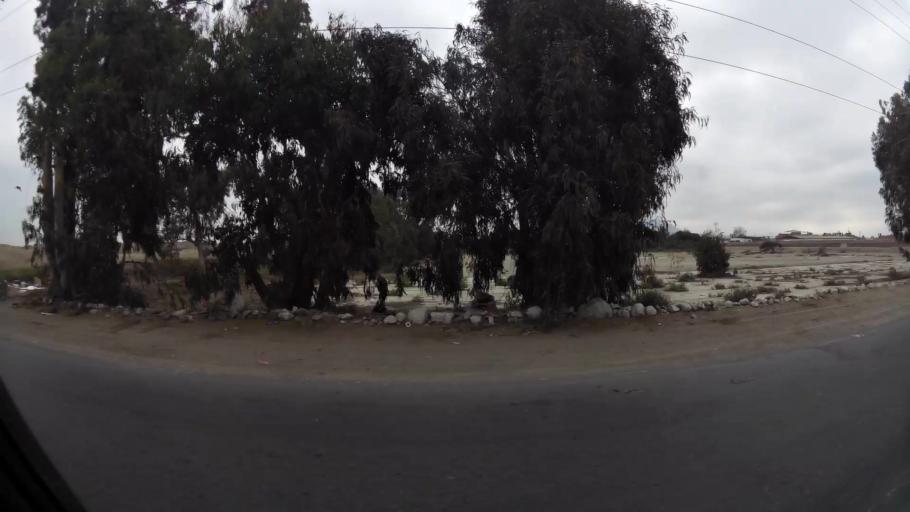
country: PE
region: La Libertad
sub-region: Provincia de Trujillo
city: La Esperanza
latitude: -8.0993
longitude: -79.0663
